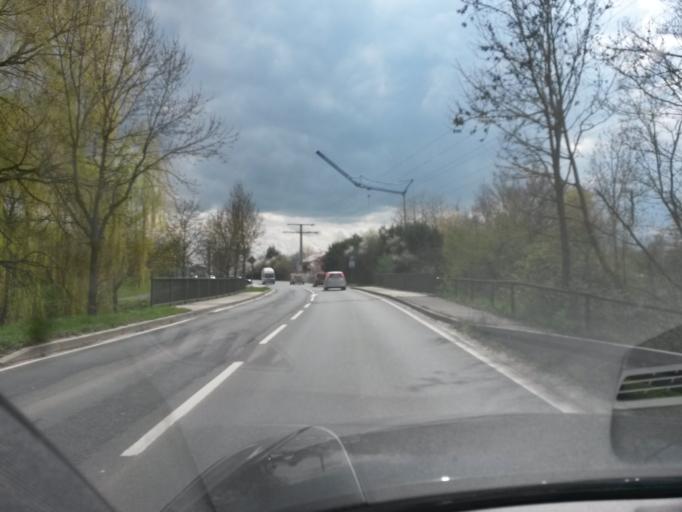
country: DE
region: Bavaria
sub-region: Regierungsbezirk Unterfranken
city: Volkach
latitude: 49.8635
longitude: 10.2240
